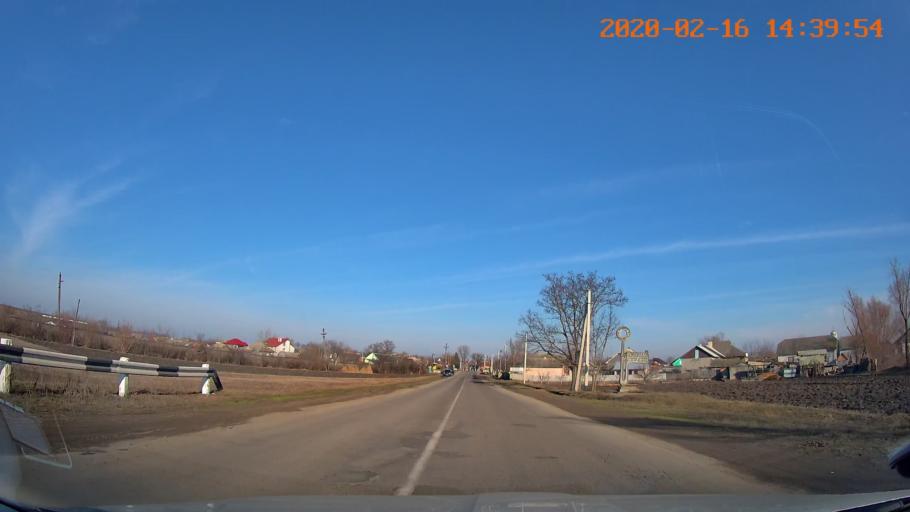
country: RO
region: Botosani
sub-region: Comuna Darabani
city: Bajura
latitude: 48.2472
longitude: 26.5545
